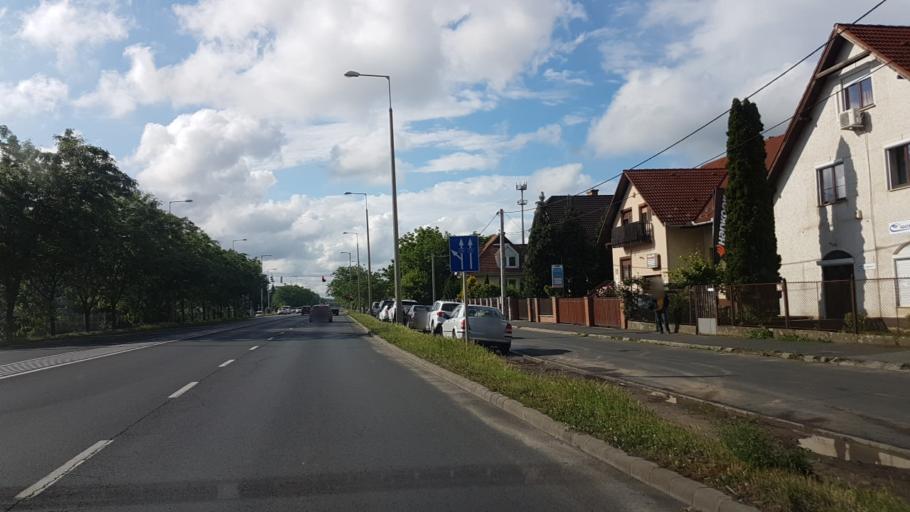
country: HU
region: Hajdu-Bihar
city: Debrecen
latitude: 47.5569
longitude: 21.6058
